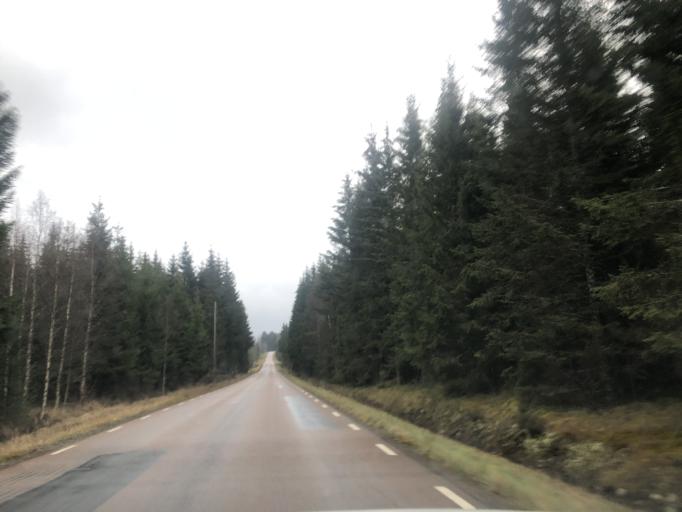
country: SE
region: Vaestra Goetaland
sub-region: Ulricehamns Kommun
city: Ulricehamn
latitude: 57.8275
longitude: 13.5081
